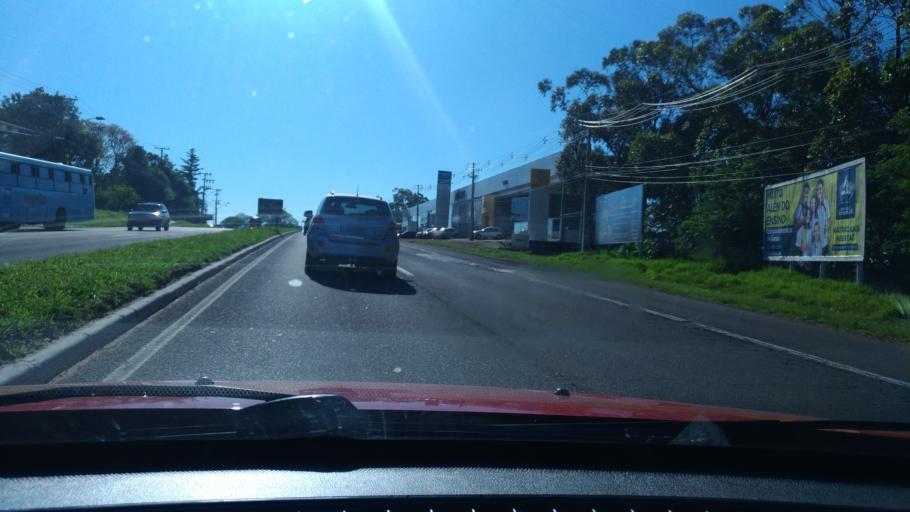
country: BR
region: Rio Grande do Sul
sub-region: Viamao
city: Viamao
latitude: -30.0932
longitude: -51.0750
